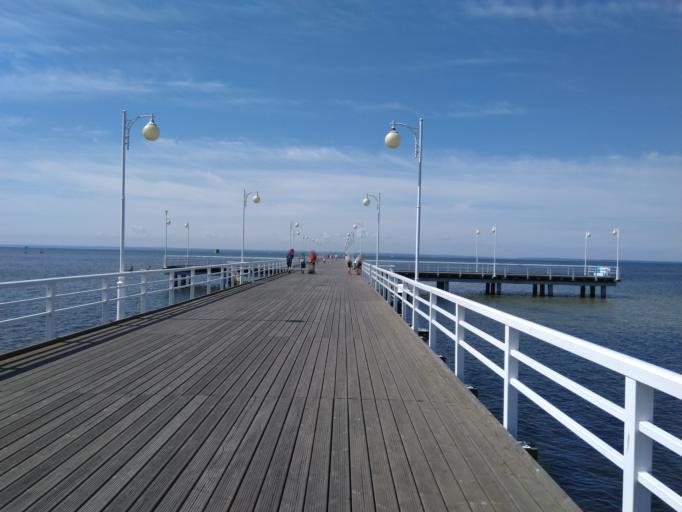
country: PL
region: Pomeranian Voivodeship
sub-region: Powiat pucki
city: Jastarnia
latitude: 54.6815
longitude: 18.7099
